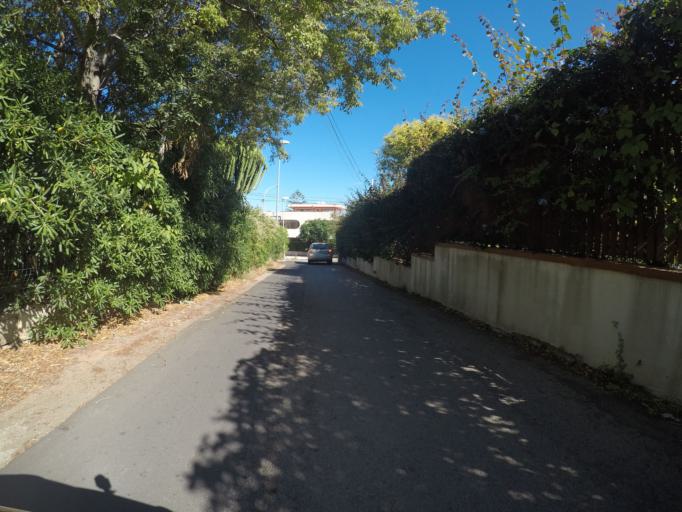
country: IT
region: Sicily
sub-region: Palermo
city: Palermo
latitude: 38.1888
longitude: 13.3473
